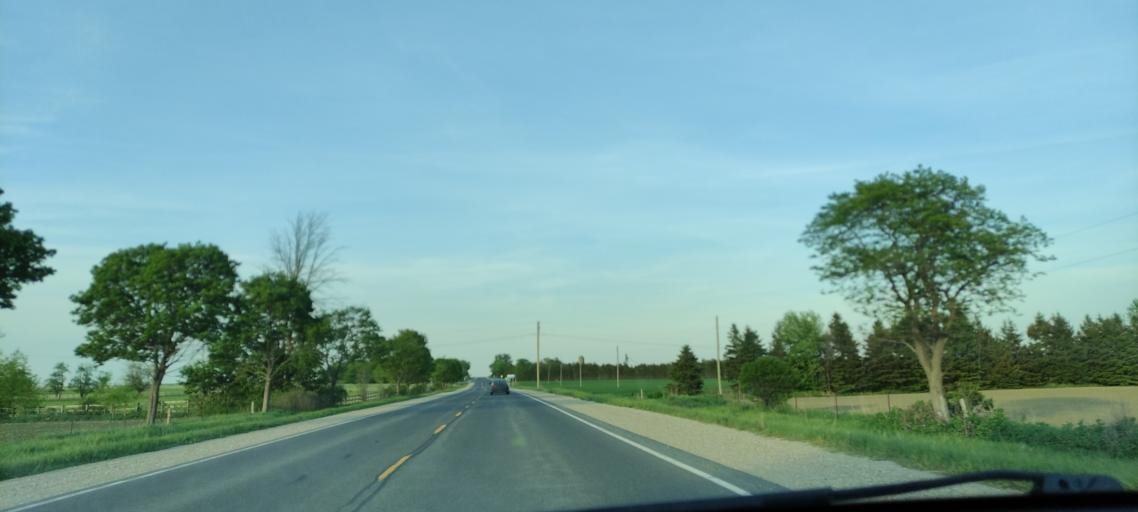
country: CA
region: Ontario
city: London
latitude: 43.1967
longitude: -81.2471
